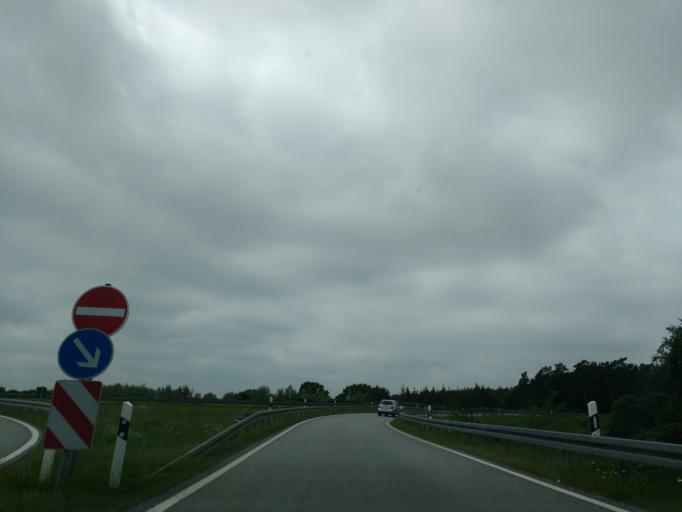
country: DE
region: Mecklenburg-Vorpommern
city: Zurow
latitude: 53.8719
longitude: 11.6216
